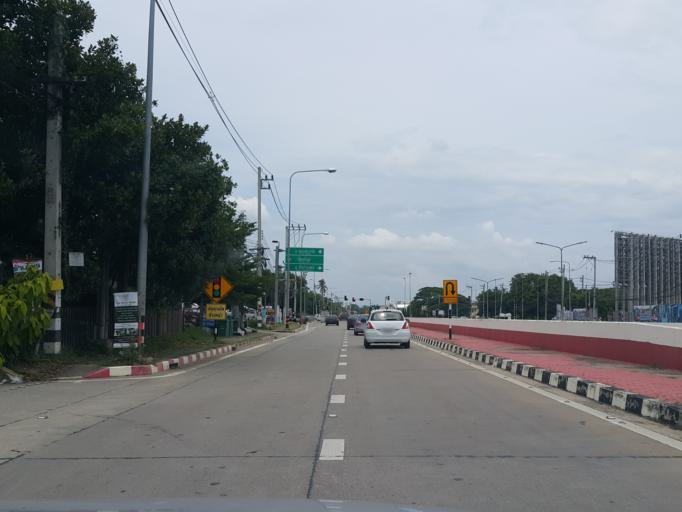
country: TH
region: Chiang Mai
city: Chiang Mai
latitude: 18.7784
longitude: 99.0421
